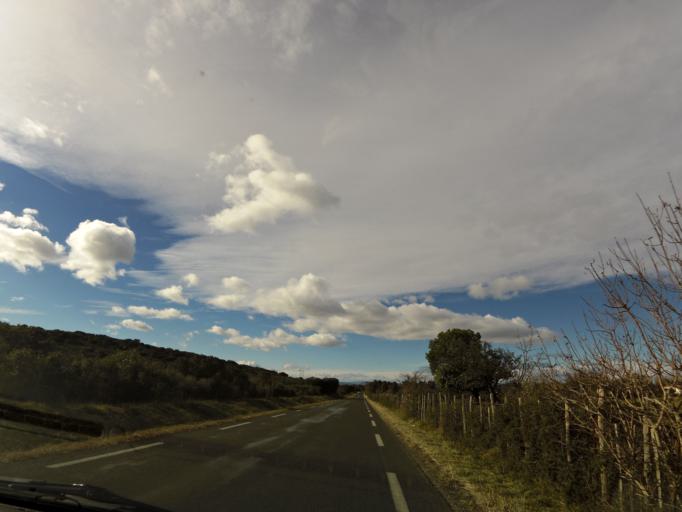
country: FR
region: Languedoc-Roussillon
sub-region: Departement du Gard
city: Aubais
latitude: 43.7528
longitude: 4.1196
